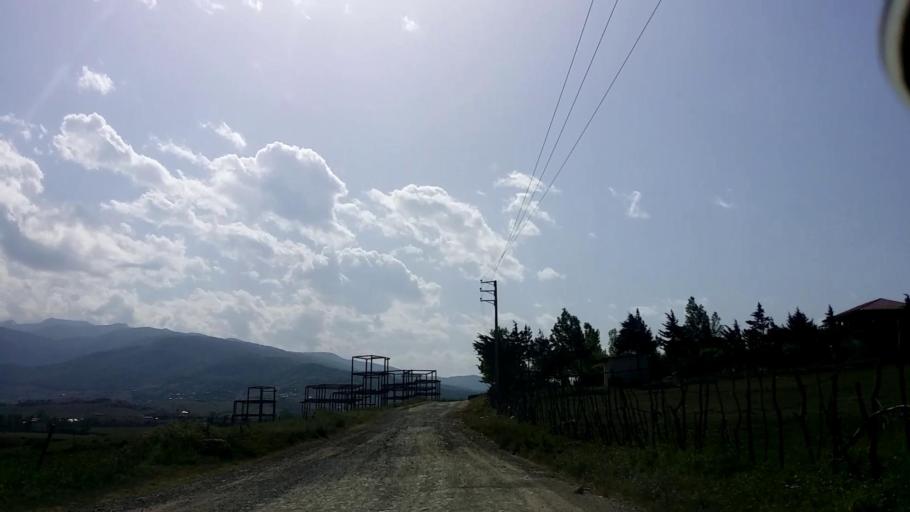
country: IR
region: Mazandaran
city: `Abbasabad
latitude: 36.5427
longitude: 51.2032
